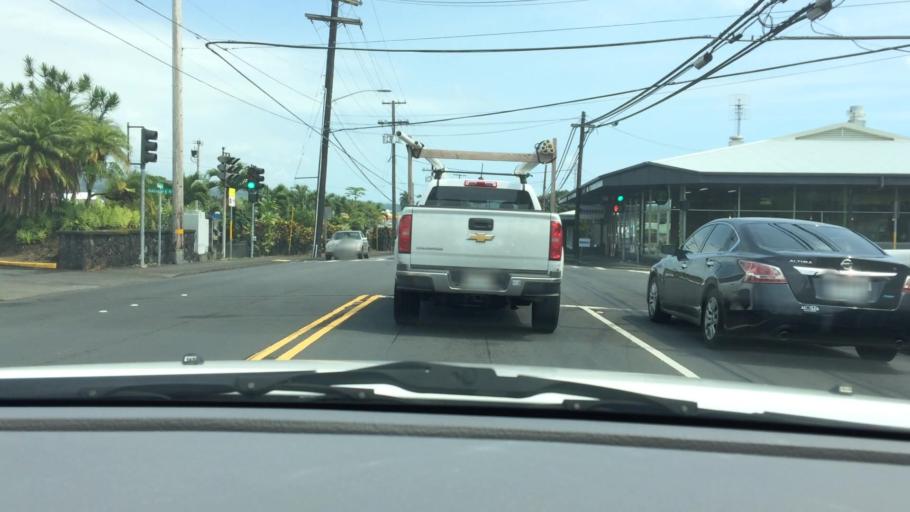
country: US
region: Hawaii
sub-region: Hawaii County
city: Hilo
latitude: 19.7112
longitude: -155.0767
